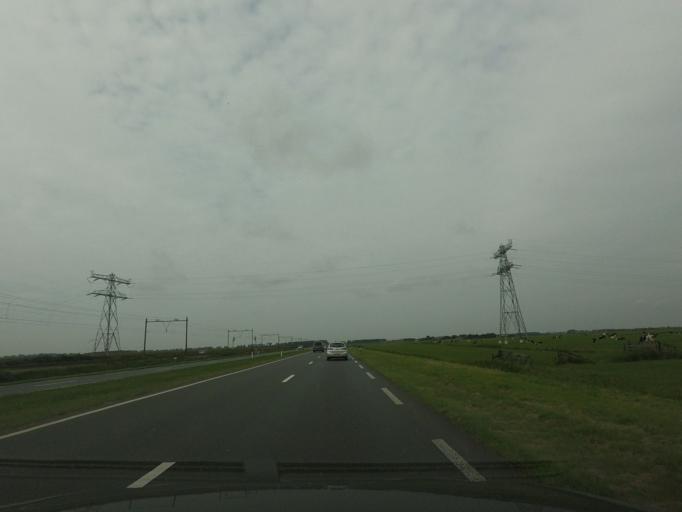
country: NL
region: North Holland
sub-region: Gemeente Uitgeest
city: Uitgeest
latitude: 52.5045
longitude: 4.7356
